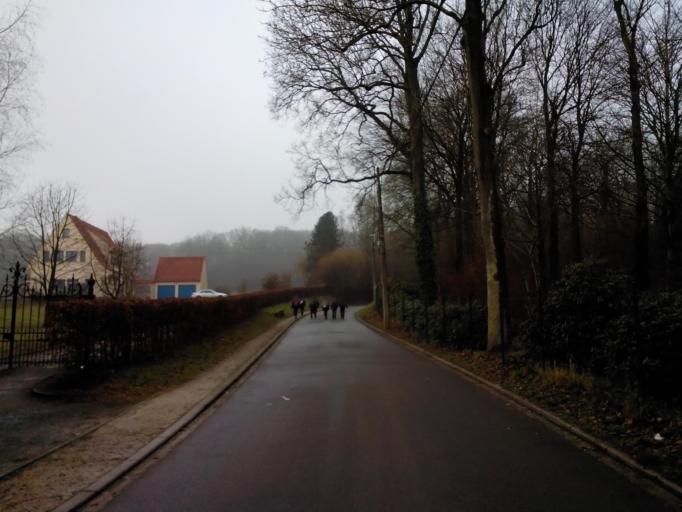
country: BE
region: Wallonia
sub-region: Province du Brabant Wallon
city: Grez-Doiceau
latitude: 50.7486
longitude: 4.6723
